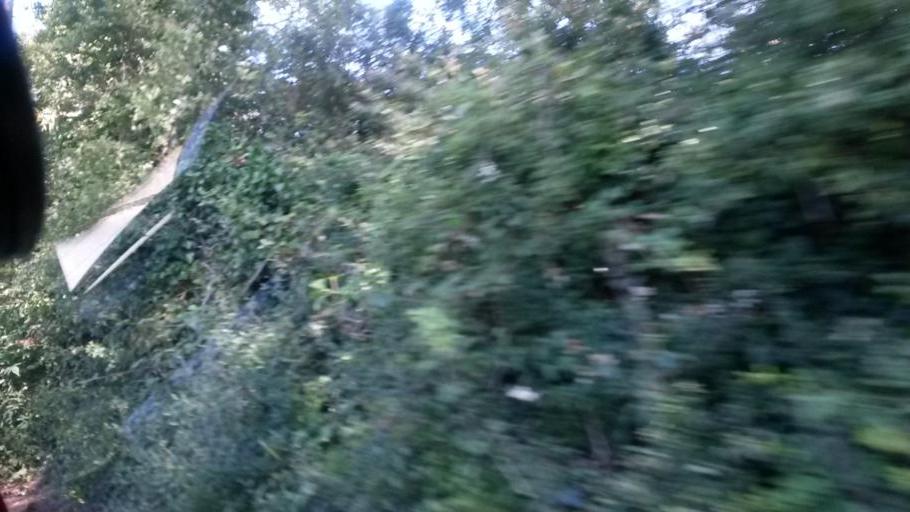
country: IE
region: Leinster
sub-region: An Mhi
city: Ashbourne
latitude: 53.5232
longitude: -6.3151
